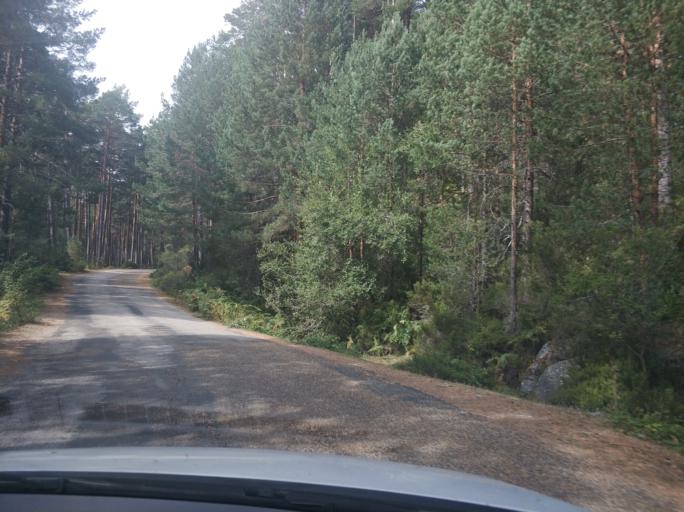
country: ES
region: Castille and Leon
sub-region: Provincia de Soria
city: Duruelo de la Sierra
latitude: 41.9960
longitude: -2.9128
